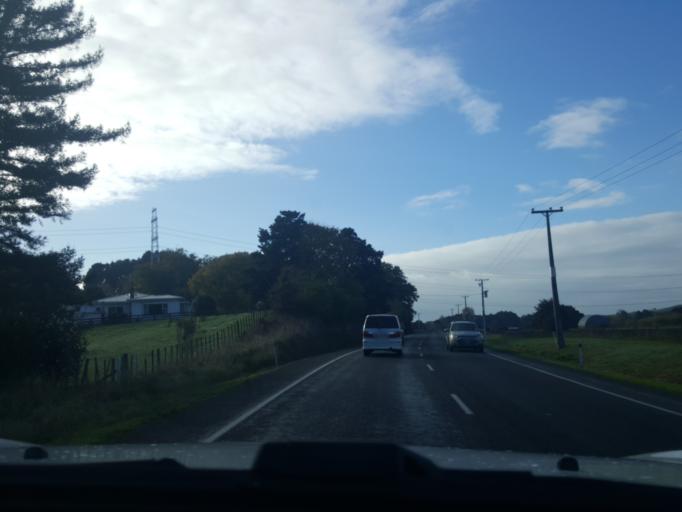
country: NZ
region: Waikato
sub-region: Waipa District
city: Cambridge
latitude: -37.6653
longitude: 175.5013
